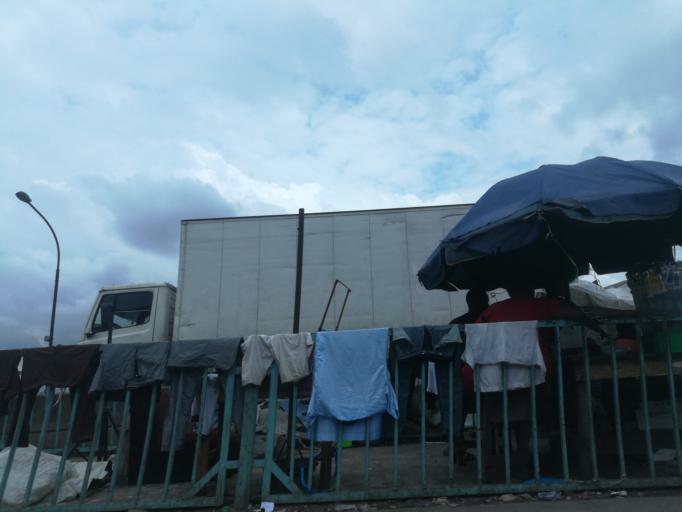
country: NG
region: Lagos
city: Lagos
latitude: 6.4630
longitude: 3.3837
